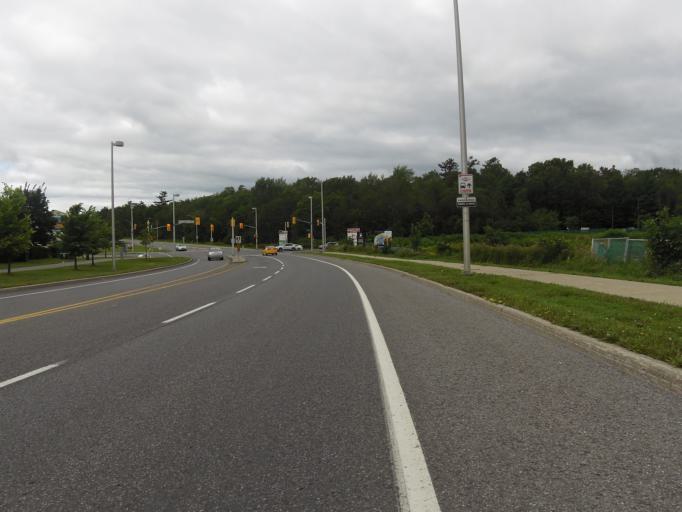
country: CA
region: Ontario
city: Bells Corners
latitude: 45.3121
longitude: -75.9042
